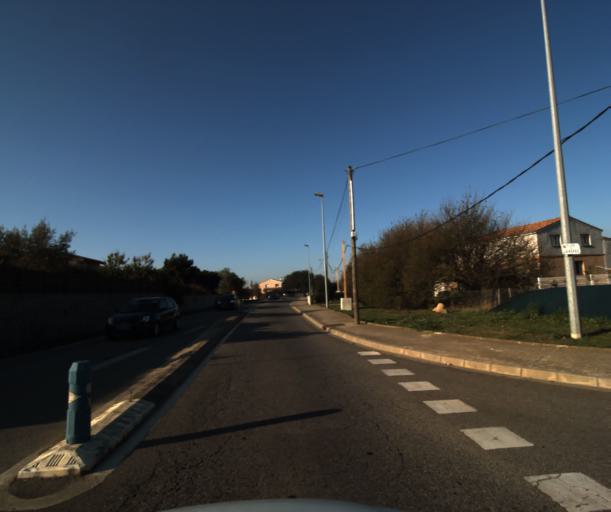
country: FR
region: Midi-Pyrenees
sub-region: Departement de la Haute-Garonne
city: Colomiers
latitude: 43.6222
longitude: 1.3341
